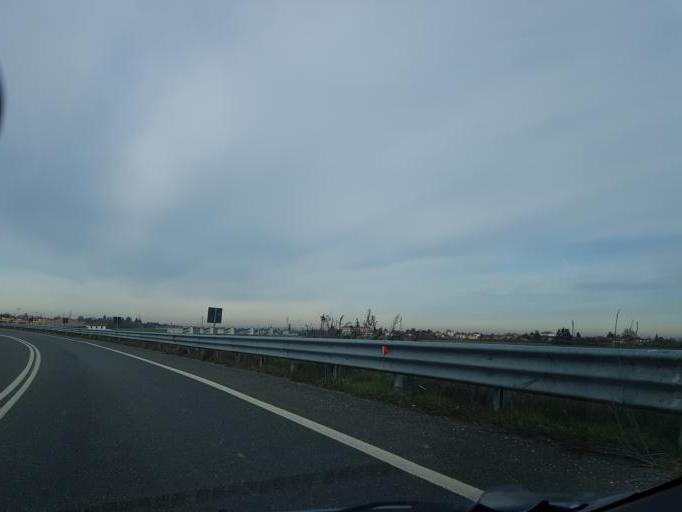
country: IT
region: Piedmont
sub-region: Provincia di Alessandria
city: Novi Ligure
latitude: 44.7561
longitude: 8.8202
